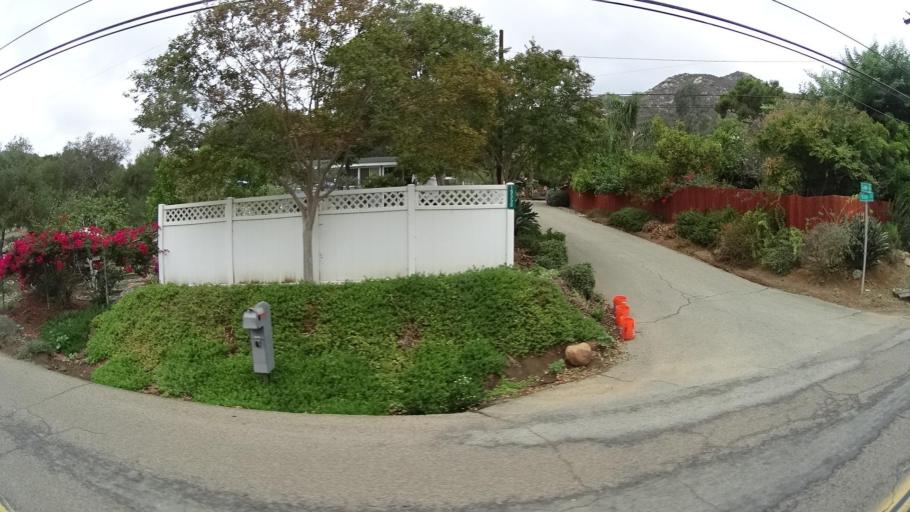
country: US
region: California
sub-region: San Diego County
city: Escondido
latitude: 33.0661
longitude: -117.1202
